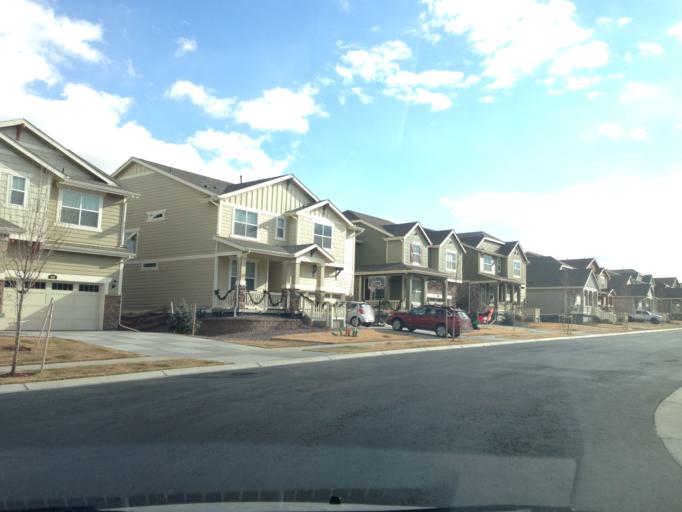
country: US
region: Colorado
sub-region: Boulder County
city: Erie
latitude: 40.0360
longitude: -105.0869
